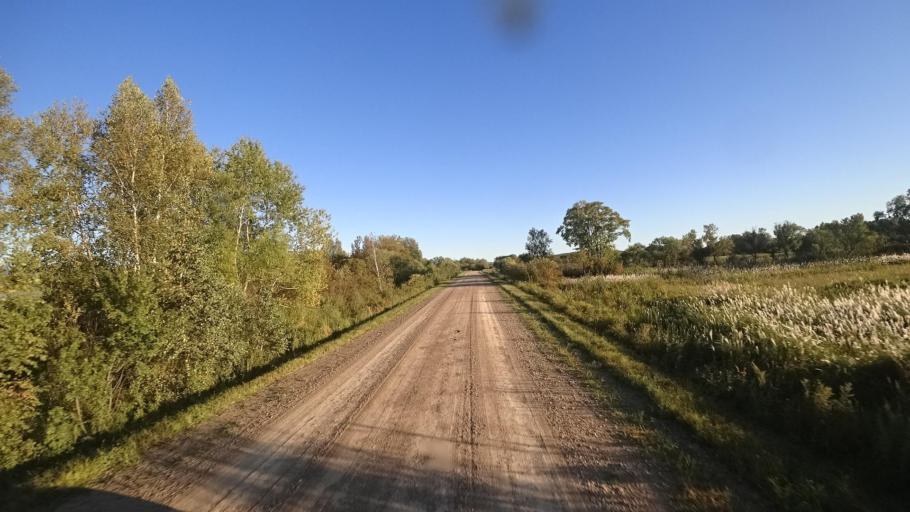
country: RU
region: Primorskiy
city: Kirovskiy
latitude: 44.7855
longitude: 133.6243
